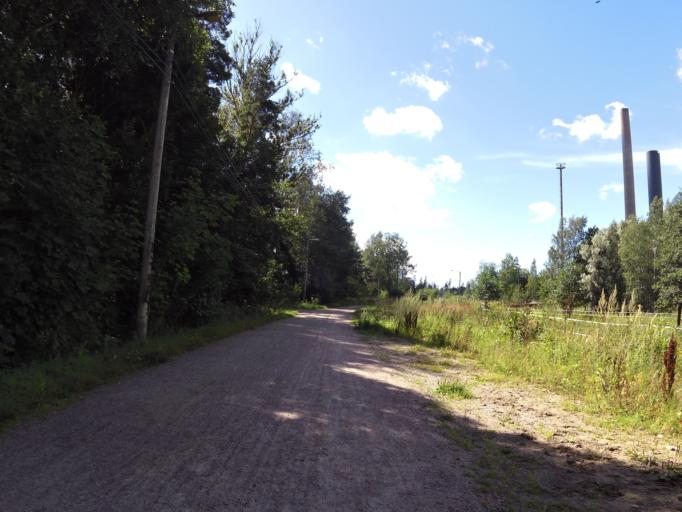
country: FI
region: Uusimaa
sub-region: Helsinki
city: Koukkuniemi
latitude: 60.1507
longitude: 24.7241
